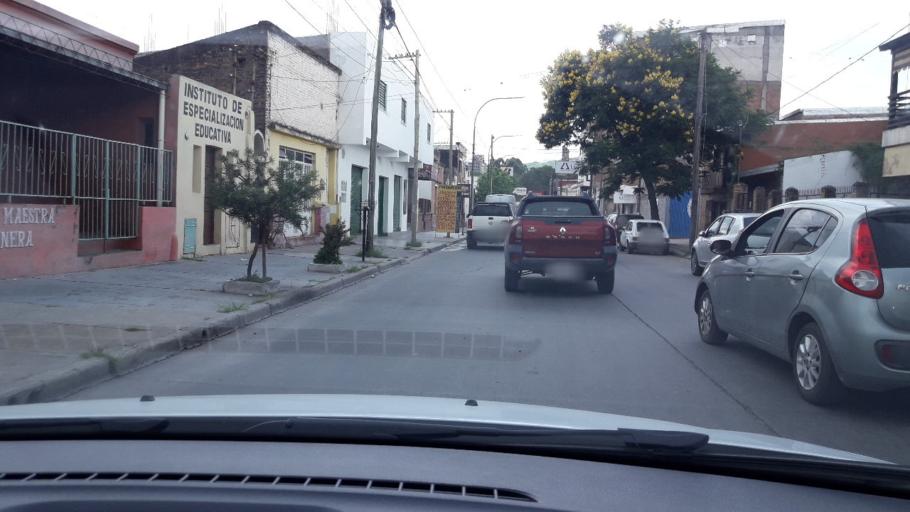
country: AR
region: Jujuy
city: San Salvador de Jujuy
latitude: -24.1923
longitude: -65.2908
